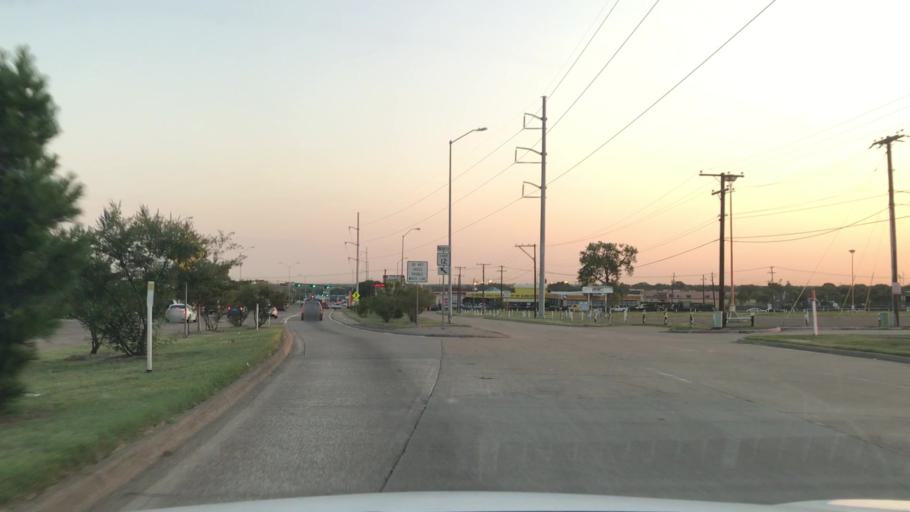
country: US
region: Texas
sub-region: Dallas County
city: Mesquite
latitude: 32.8008
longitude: -96.6822
